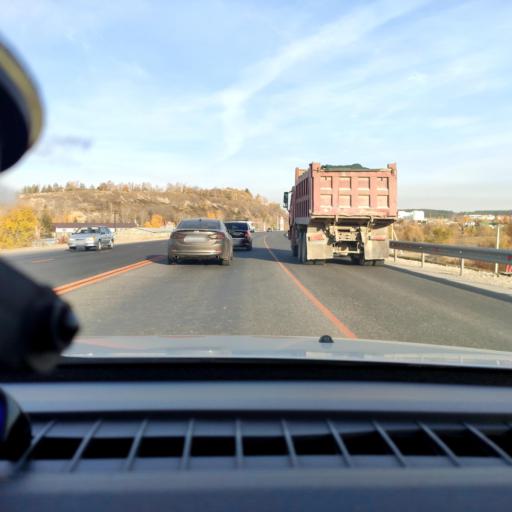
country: RU
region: Samara
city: Volzhskiy
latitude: 53.4175
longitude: 50.1291
